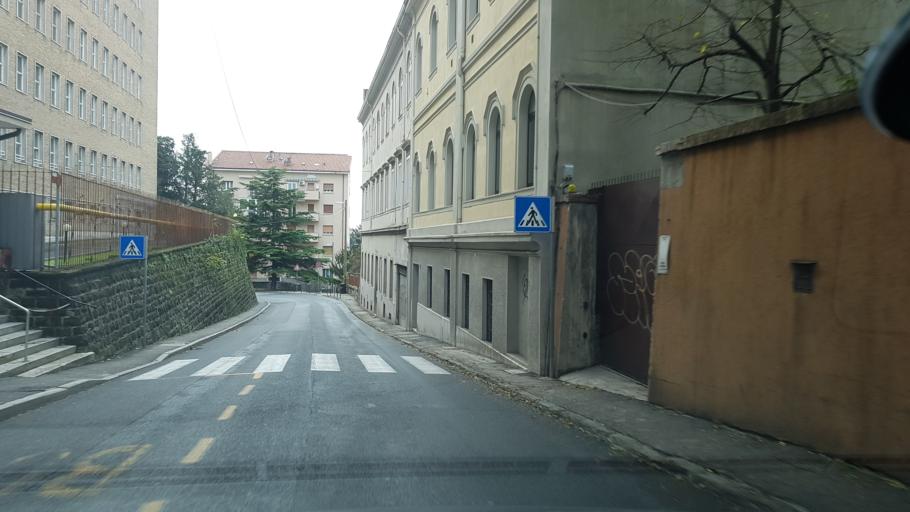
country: IT
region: Friuli Venezia Giulia
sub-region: Provincia di Trieste
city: Trieste
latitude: 45.6527
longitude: 13.7871
